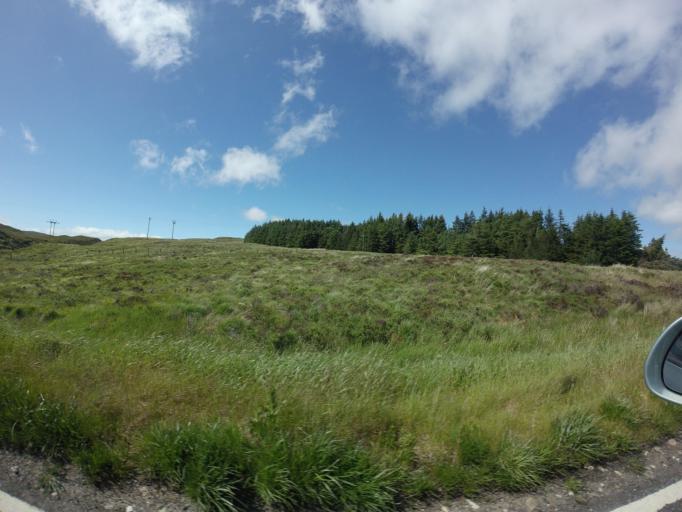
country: GB
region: Scotland
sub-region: Eilean Siar
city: Stornoway
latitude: 58.1473
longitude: -6.5069
